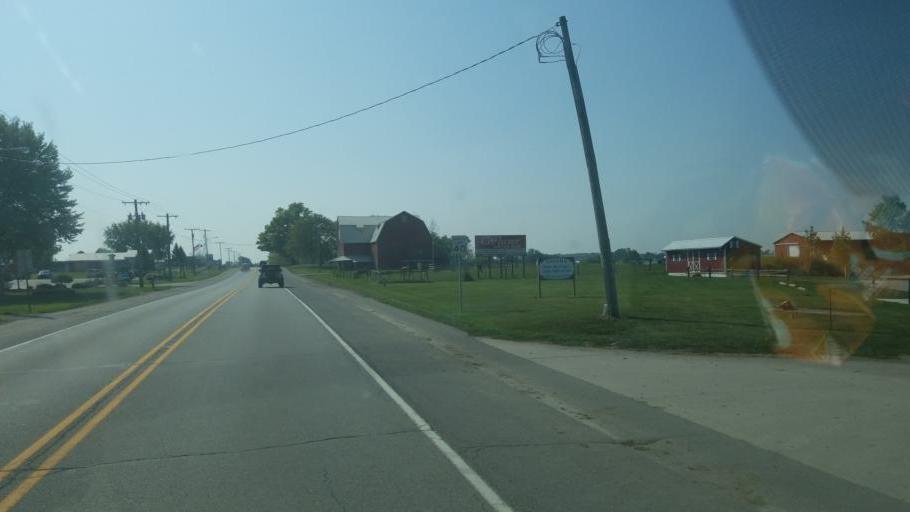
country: US
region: Indiana
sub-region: Elkhart County
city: Middlebury
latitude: 41.6643
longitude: -85.5804
